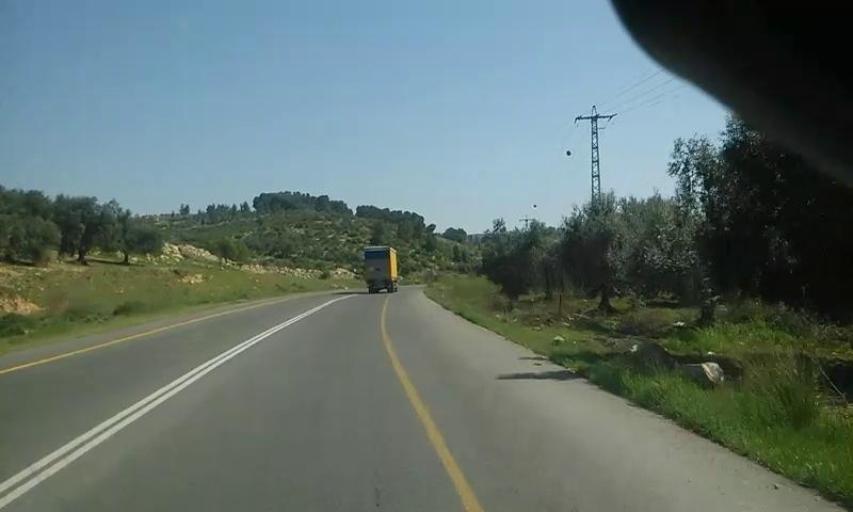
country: PS
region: West Bank
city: Idhna
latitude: 31.5738
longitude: 34.9818
